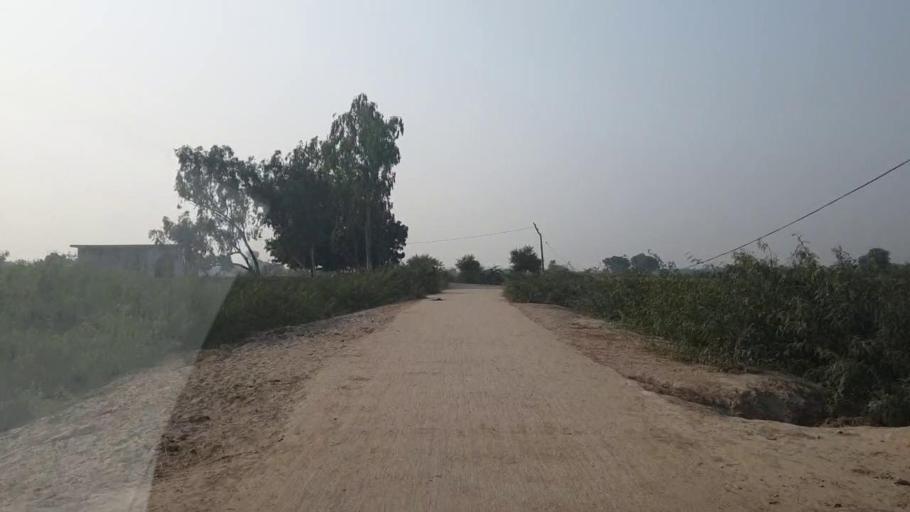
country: PK
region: Sindh
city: Tando Jam
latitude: 25.3331
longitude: 68.5264
